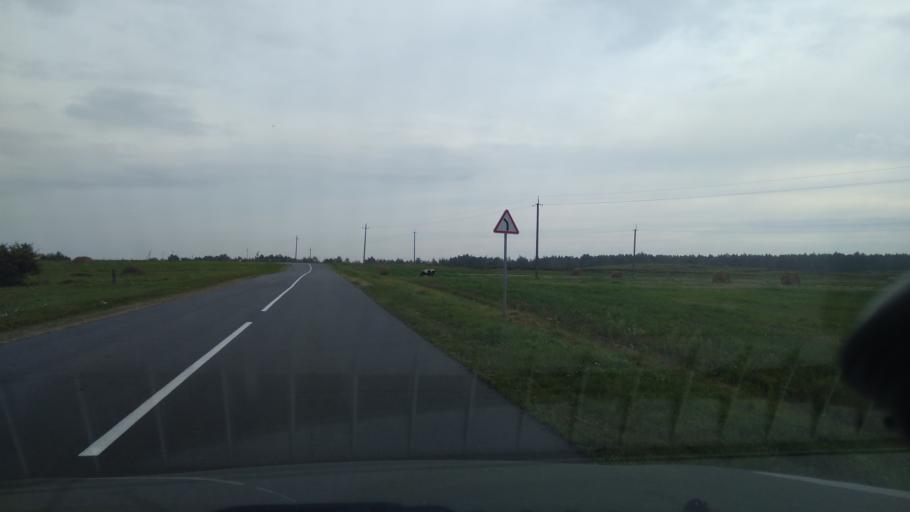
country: BY
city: Michanovichi
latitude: 53.6148
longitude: 27.7143
